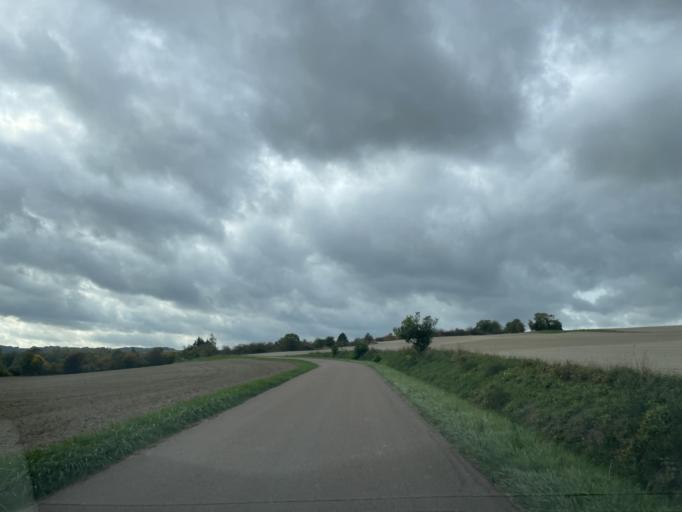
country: FR
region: Bourgogne
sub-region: Departement de l'Yonne
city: Aillant-sur-Tholon
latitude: 47.8294
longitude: 3.3462
